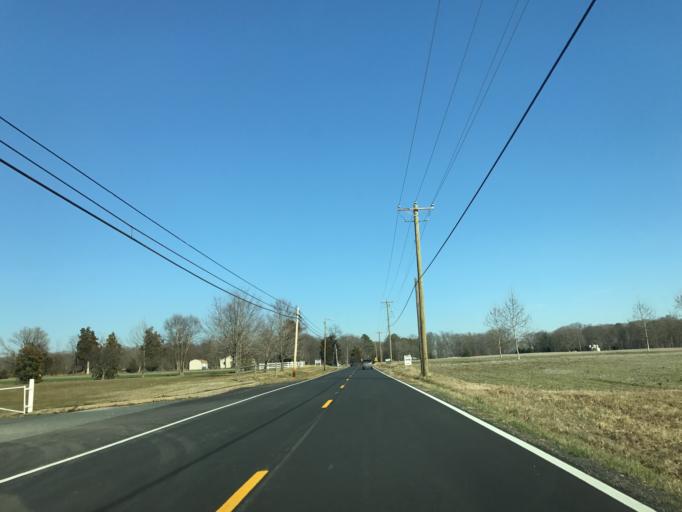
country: US
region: Maryland
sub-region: Queen Anne's County
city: Centreville
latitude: 39.0280
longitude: -76.1054
